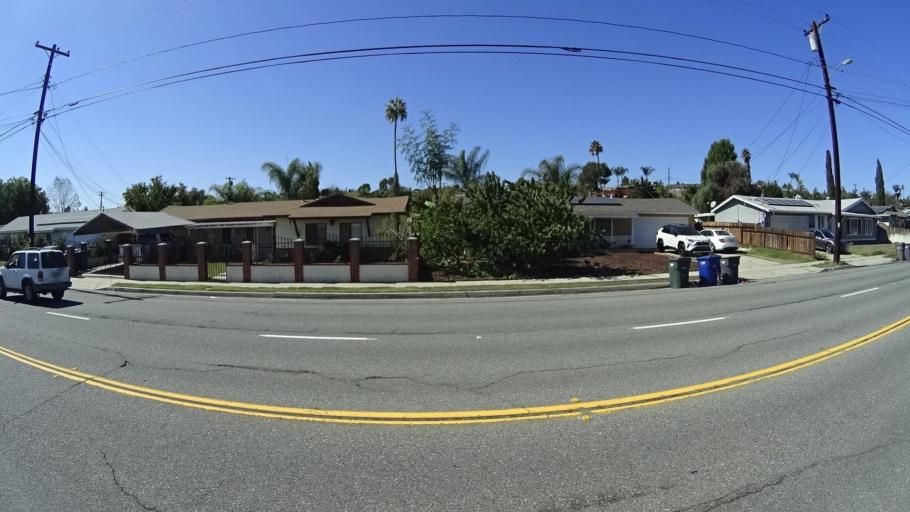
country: US
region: California
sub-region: San Diego County
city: La Presa
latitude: 32.7107
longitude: -117.0156
